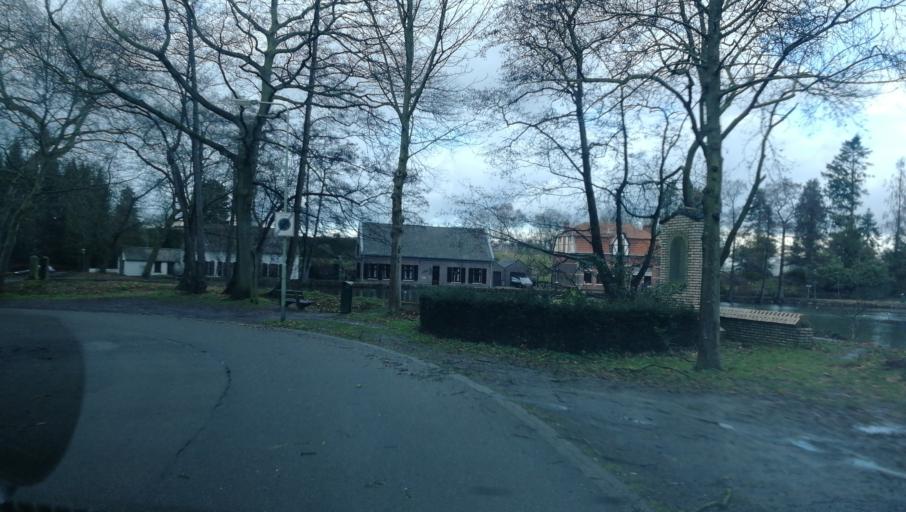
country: NL
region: Limburg
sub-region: Gemeente Venlo
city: Tegelen
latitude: 51.3306
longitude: 6.1343
